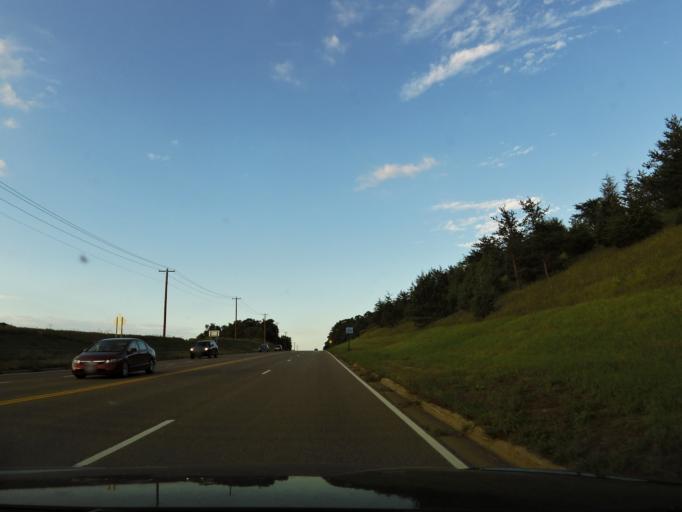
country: US
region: Minnesota
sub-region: Washington County
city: Cottage Grove
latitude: 44.8077
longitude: -92.9107
